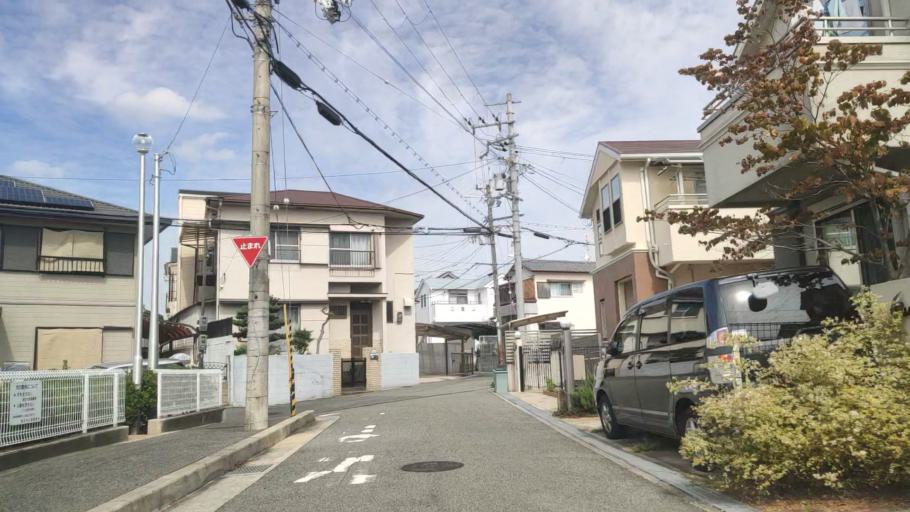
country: JP
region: Osaka
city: Mino
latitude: 34.8136
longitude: 135.4648
